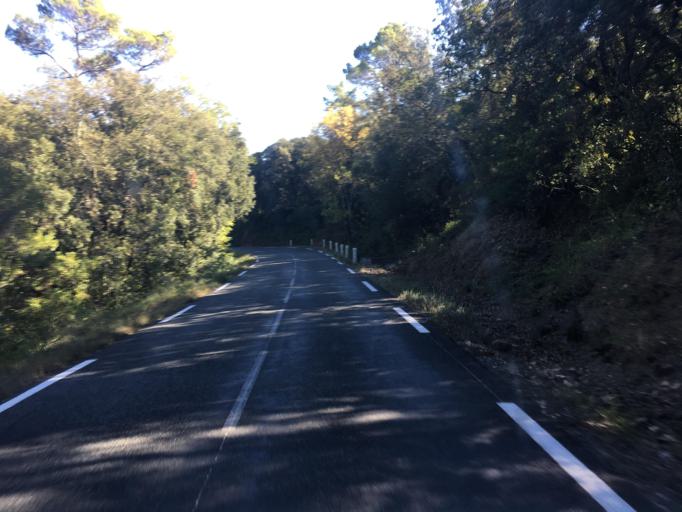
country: FR
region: Languedoc-Roussillon
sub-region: Departement de l'Herault
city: Nebian
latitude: 43.6129
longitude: 3.3793
